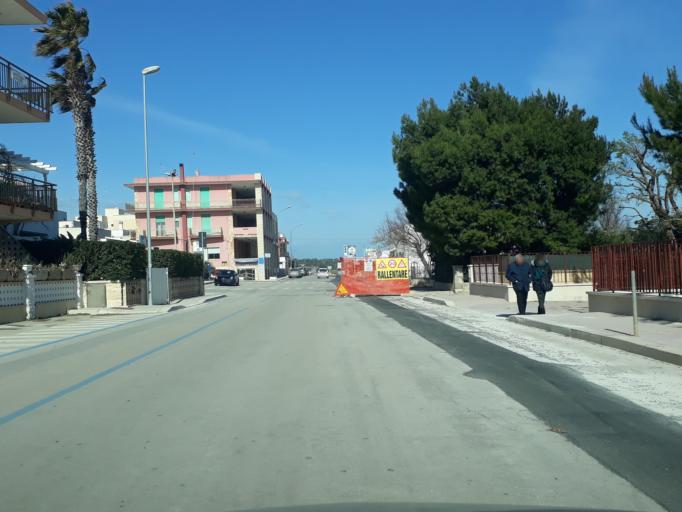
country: IT
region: Apulia
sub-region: Provincia di Bari
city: Monopoli
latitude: 40.9060
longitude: 17.3487
